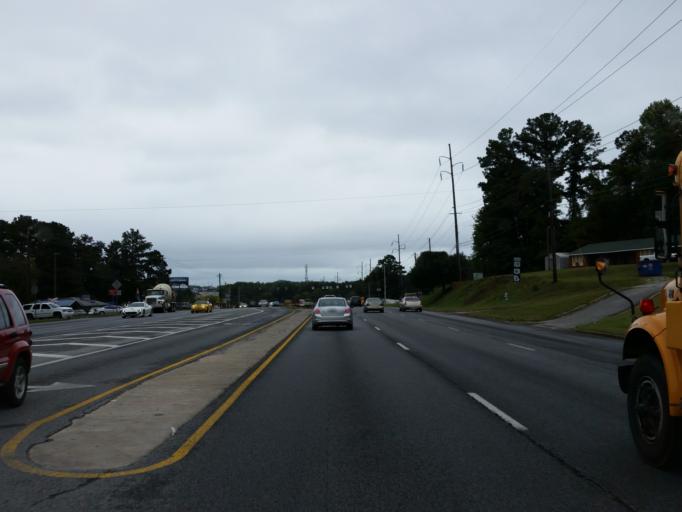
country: US
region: Georgia
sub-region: Clayton County
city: Jonesboro
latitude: 33.5499
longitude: -84.3700
